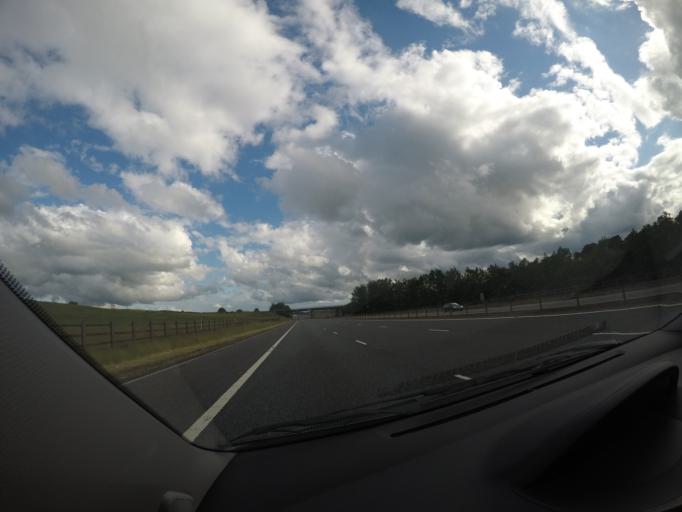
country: GB
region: Scotland
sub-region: Dumfries and Galloway
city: Lochmaben
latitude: 55.2116
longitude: -3.4125
